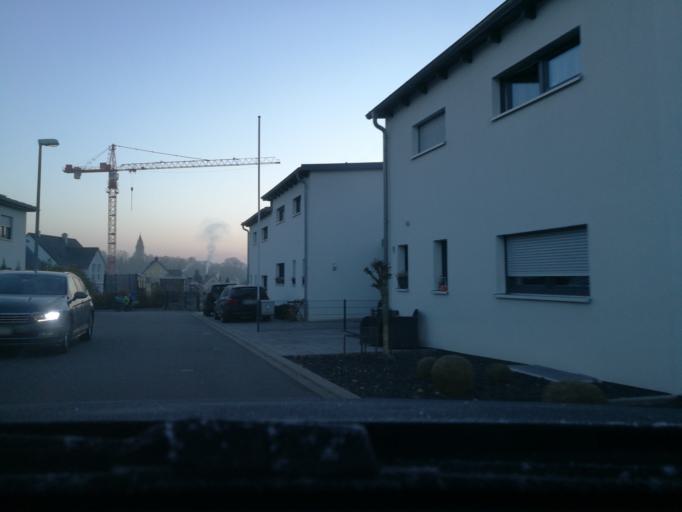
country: DE
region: Bavaria
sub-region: Regierungsbezirk Mittelfranken
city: Veitsbronn
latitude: 49.5129
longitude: 10.8784
